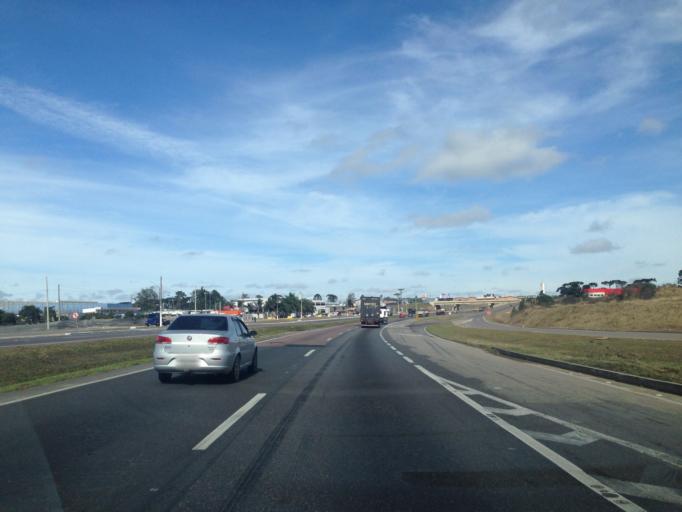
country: BR
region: Parana
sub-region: Sao Jose Dos Pinhais
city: Sao Jose dos Pinhais
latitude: -25.5556
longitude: -49.1499
